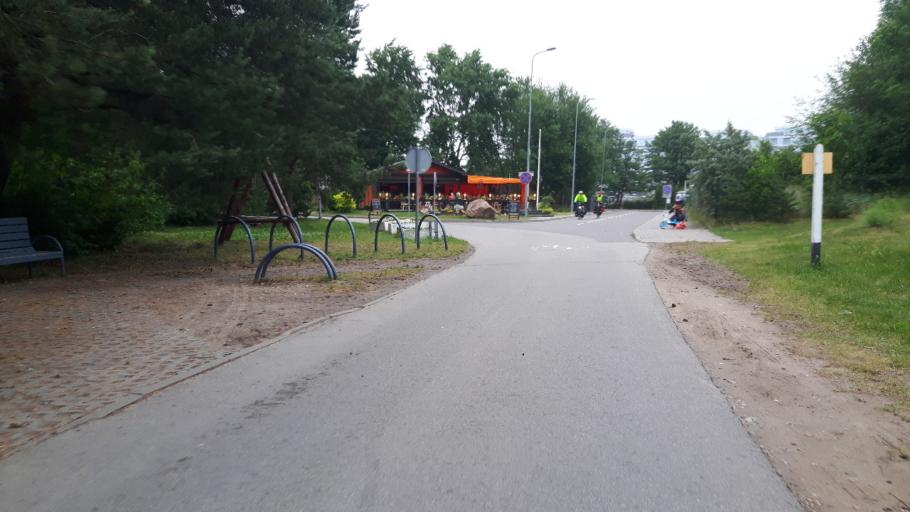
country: LT
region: Klaipedos apskritis
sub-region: Palanga
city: Sventoji
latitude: 56.0140
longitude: 21.0766
